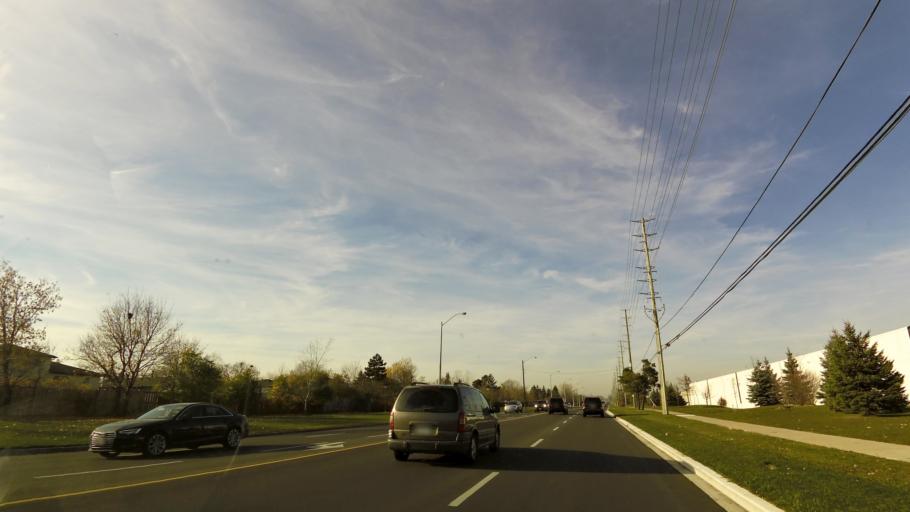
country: CA
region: Ontario
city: Brampton
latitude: 43.7391
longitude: -79.7133
